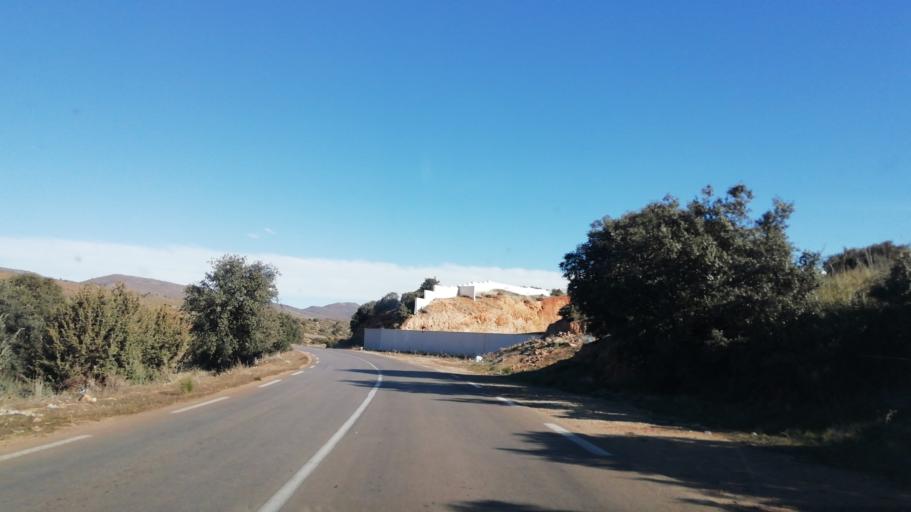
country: DZ
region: Tlemcen
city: Ouled Mimoun
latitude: 34.7598
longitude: -1.1451
